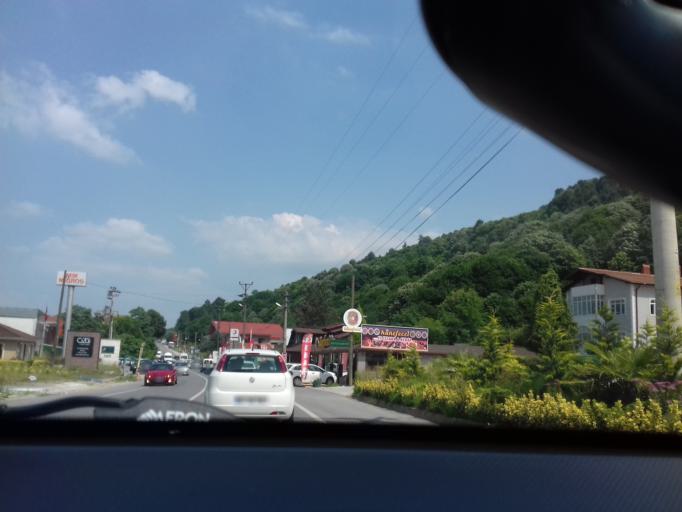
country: TR
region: Sakarya
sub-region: Merkez
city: Sapanca
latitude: 40.6908
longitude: 30.2204
